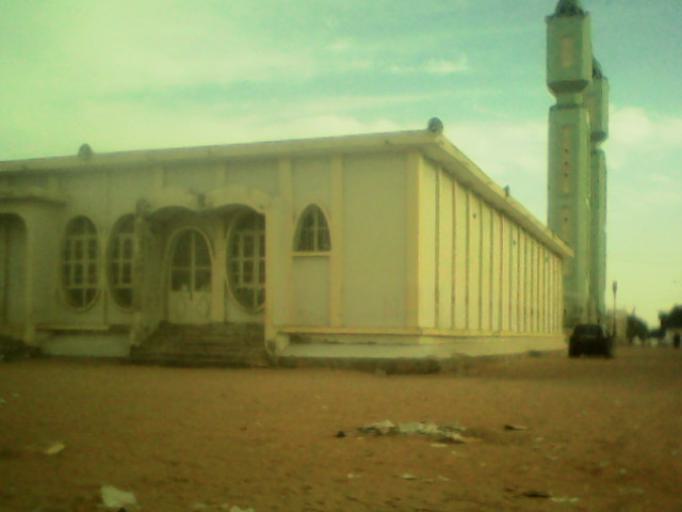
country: SN
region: Diourbel
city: Touba
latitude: 14.8658
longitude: -15.8795
